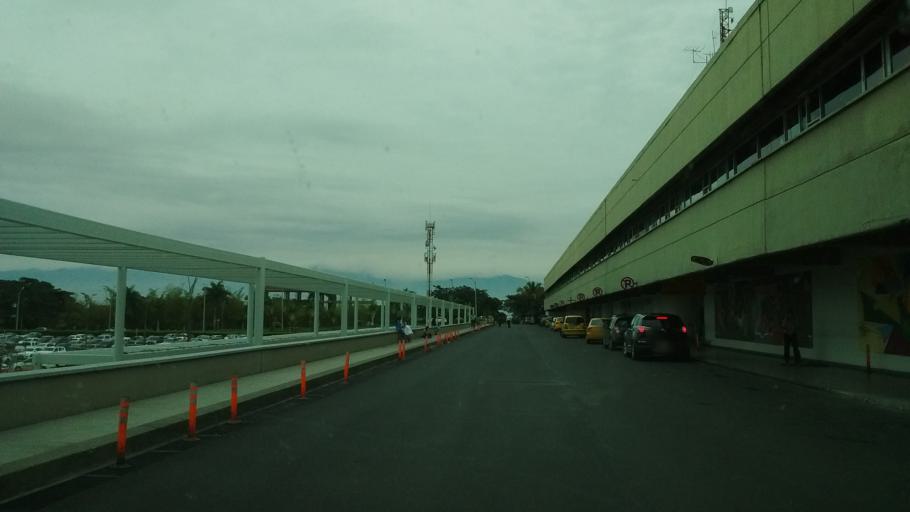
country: CO
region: Valle del Cauca
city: Palmira
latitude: 3.5362
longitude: -76.3874
